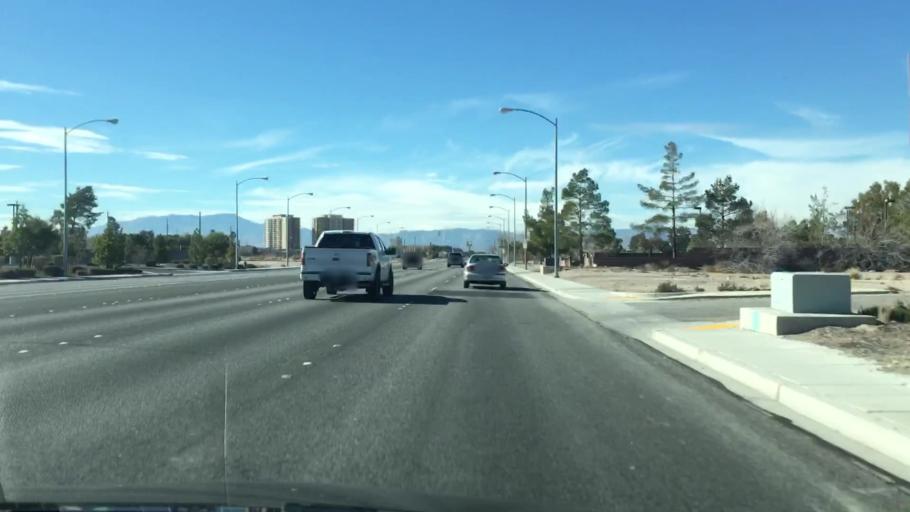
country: US
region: Nevada
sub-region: Clark County
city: Paradise
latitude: 36.0423
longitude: -115.1595
